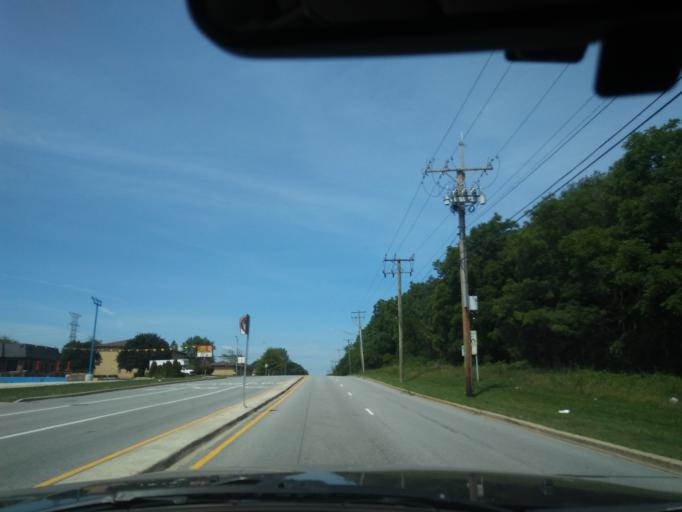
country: US
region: Illinois
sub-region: Cook County
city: Tinley Park
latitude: 41.6171
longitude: -87.7954
